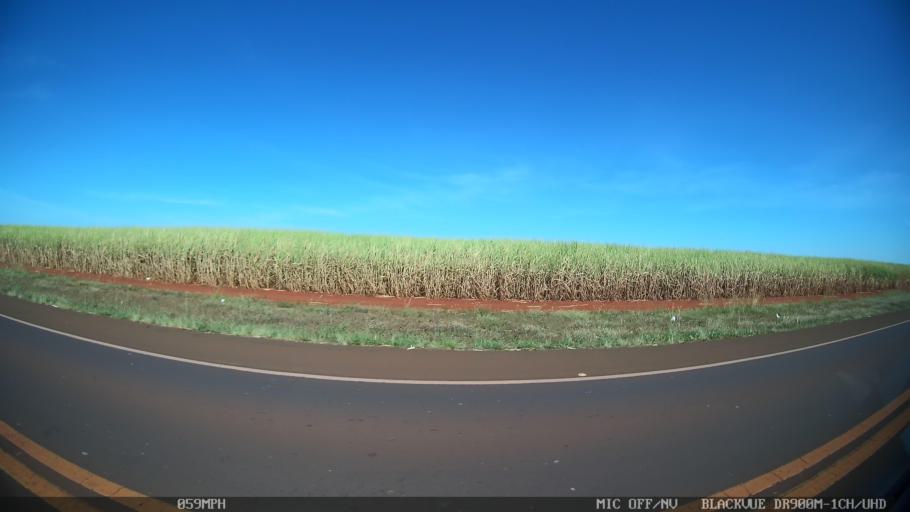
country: BR
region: Sao Paulo
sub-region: Guaira
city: Guaira
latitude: -20.4446
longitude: -48.2660
